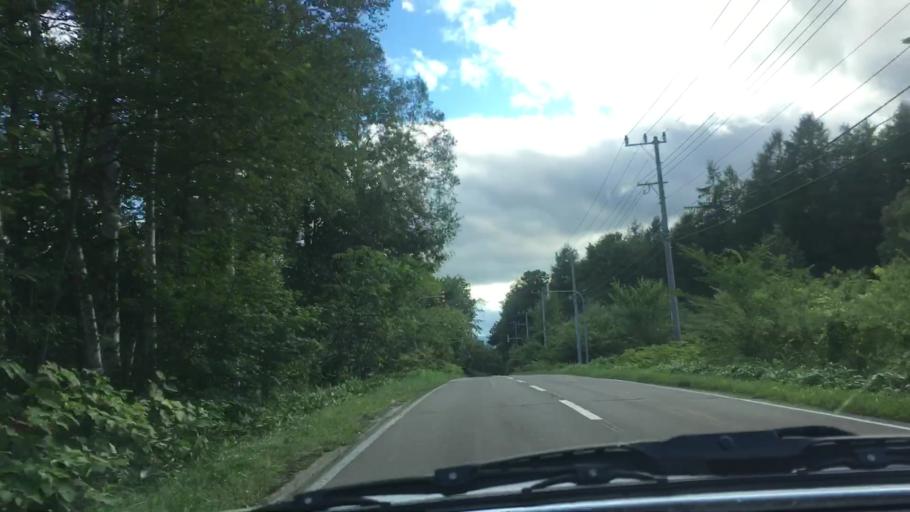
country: JP
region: Hokkaido
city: Otofuke
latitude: 43.1706
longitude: 142.9131
